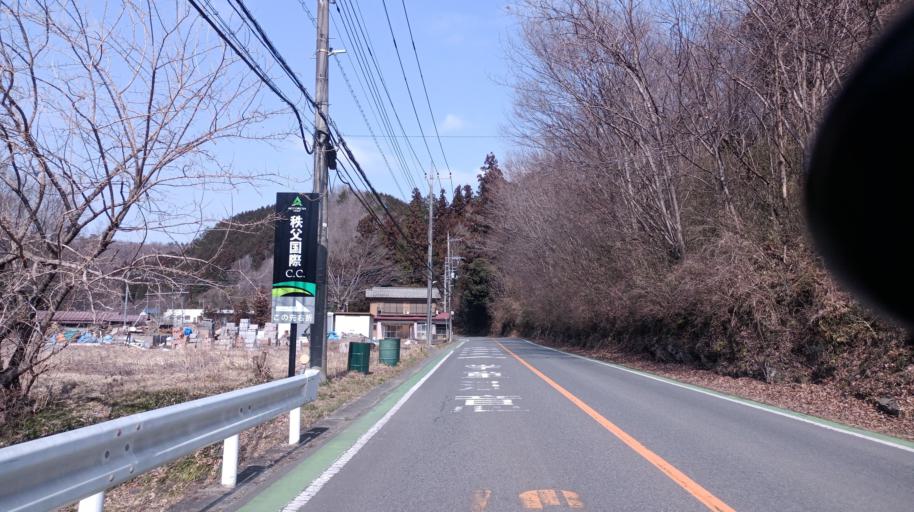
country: JP
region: Saitama
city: Yorii
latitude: 36.0641
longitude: 139.1294
